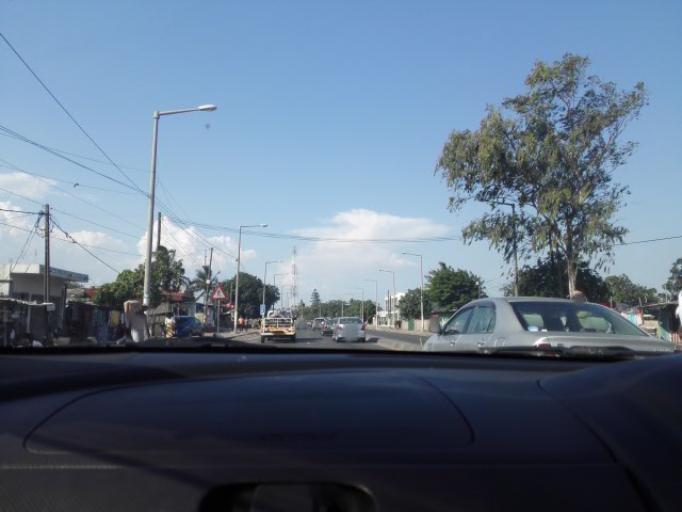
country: MZ
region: Maputo City
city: Maputo
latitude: -25.8836
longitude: 32.5670
